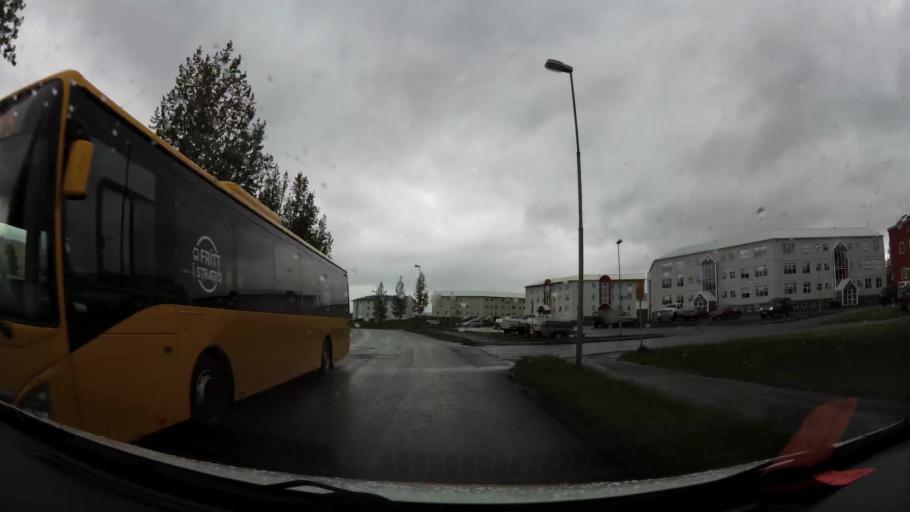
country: IS
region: Northeast
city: Akureyri
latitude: 65.6914
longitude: -18.1413
